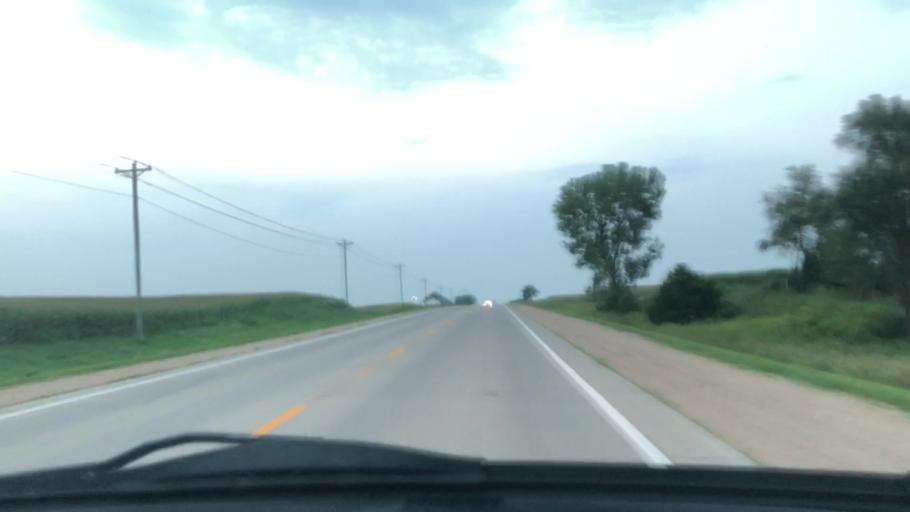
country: US
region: Iowa
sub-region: Linn County
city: Ely
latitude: 41.8518
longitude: -91.6754
